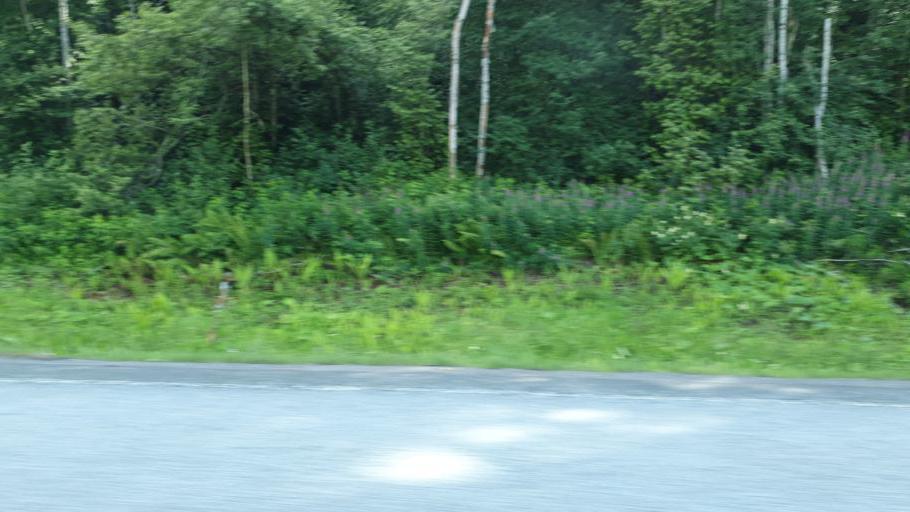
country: NO
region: Sor-Trondelag
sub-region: Midtre Gauldal
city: Storen
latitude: 63.0406
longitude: 10.2988
